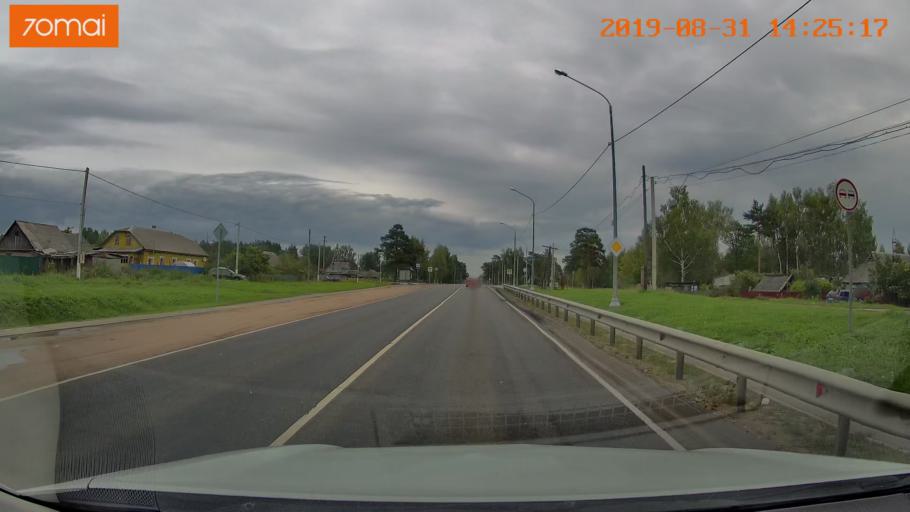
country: RU
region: Smolensk
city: Yekimovichi
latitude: 54.1075
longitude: 33.2706
